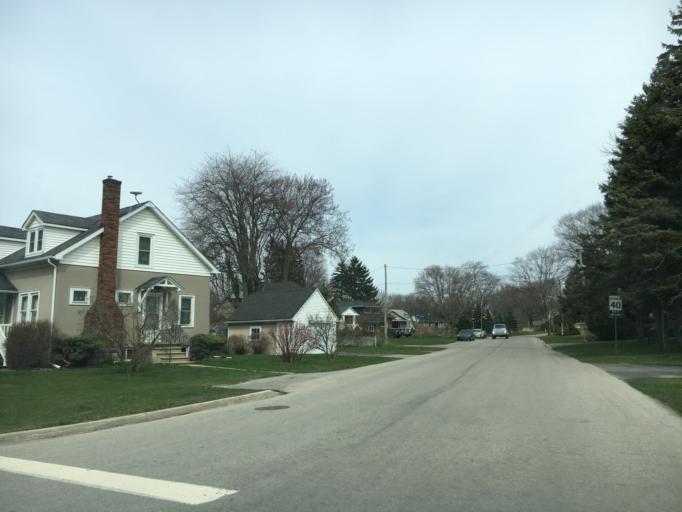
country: CA
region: Ontario
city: Port Colborne
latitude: 42.8786
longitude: -79.2701
